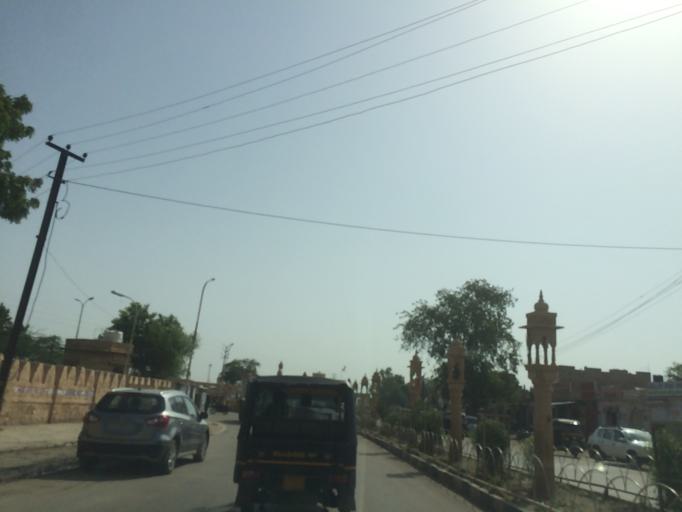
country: IN
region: Rajasthan
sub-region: Jaisalmer
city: Jaisalmer
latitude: 26.9115
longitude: 70.9227
